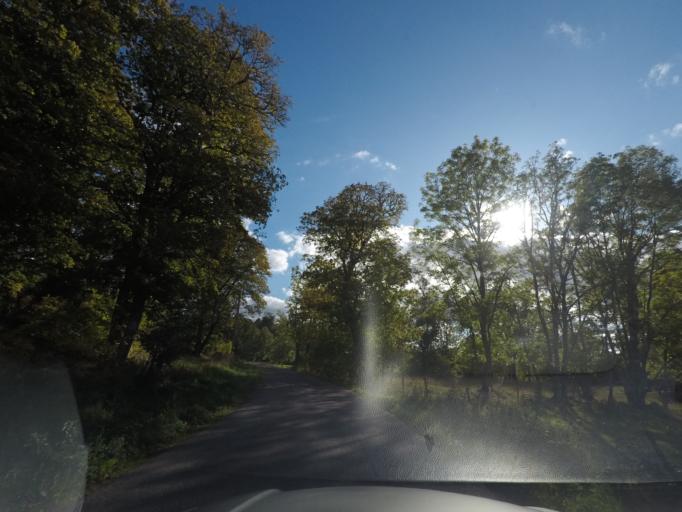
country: SE
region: Vaestmanland
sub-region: Hallstahammars Kommun
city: Kolback
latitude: 59.4978
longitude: 16.1882
